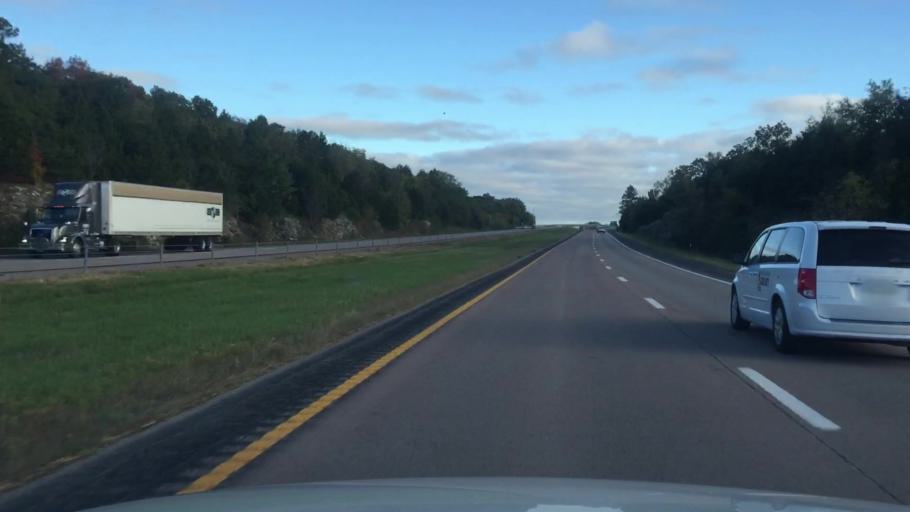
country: US
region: Missouri
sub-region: Boone County
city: Ashland
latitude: 38.8229
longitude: -92.2510
